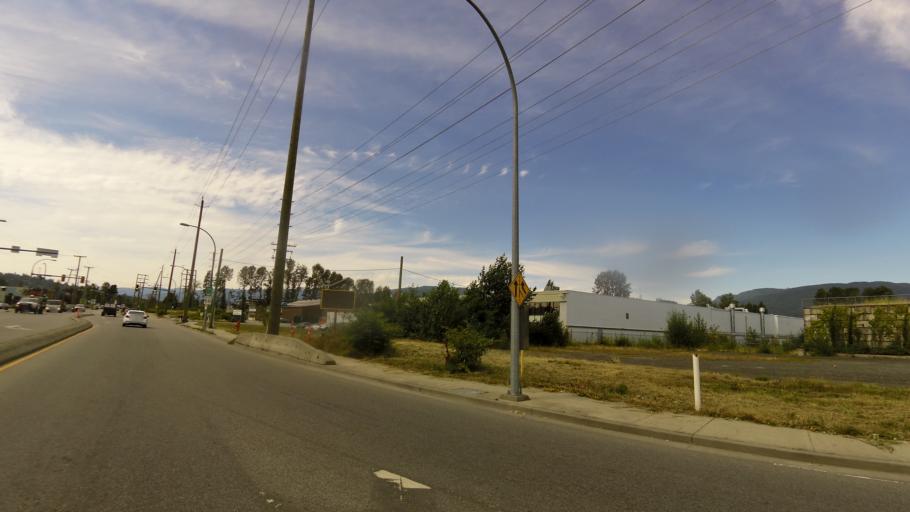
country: CA
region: British Columbia
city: Coquitlam
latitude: 49.2531
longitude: -122.7627
